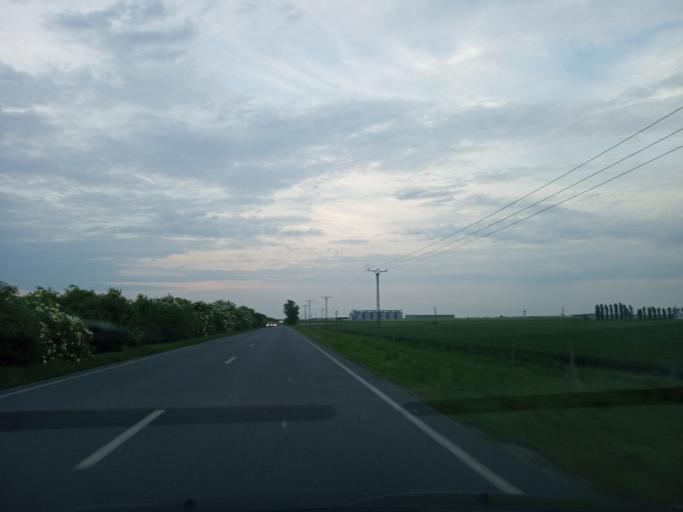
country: RO
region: Timis
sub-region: Comuna Voiteg
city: Voiteg
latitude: 45.4330
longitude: 21.2311
